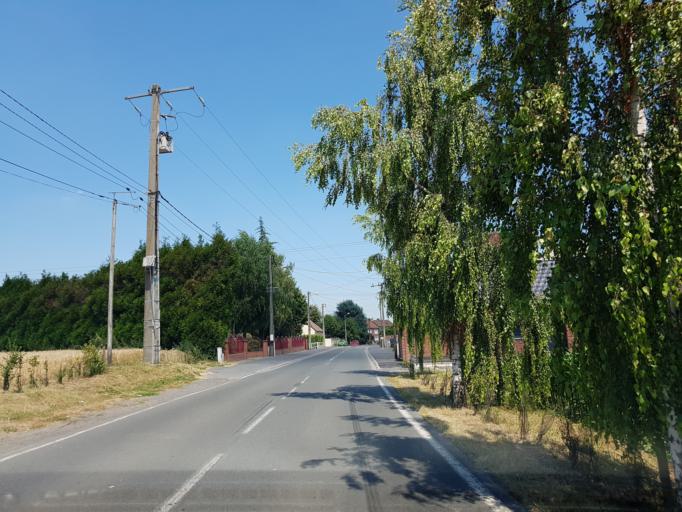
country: FR
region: Nord-Pas-de-Calais
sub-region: Departement du Nord
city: Neuville-sur-Escaut
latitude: 50.2930
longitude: 3.3563
